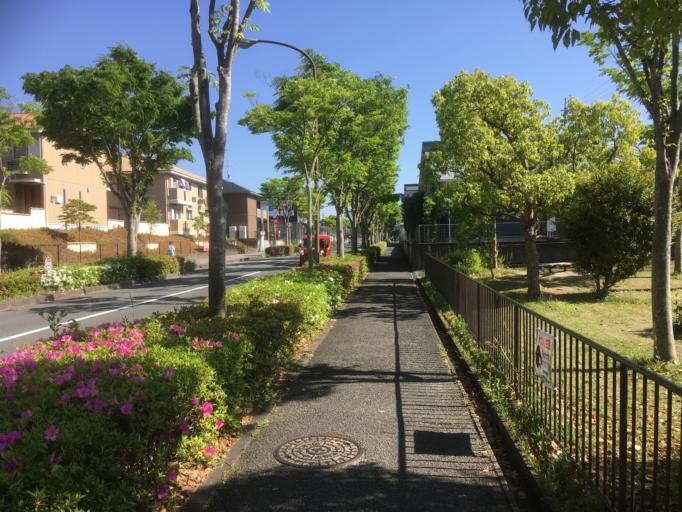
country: JP
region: Nara
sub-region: Ikoma-shi
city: Ikoma
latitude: 34.7227
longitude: 135.7159
